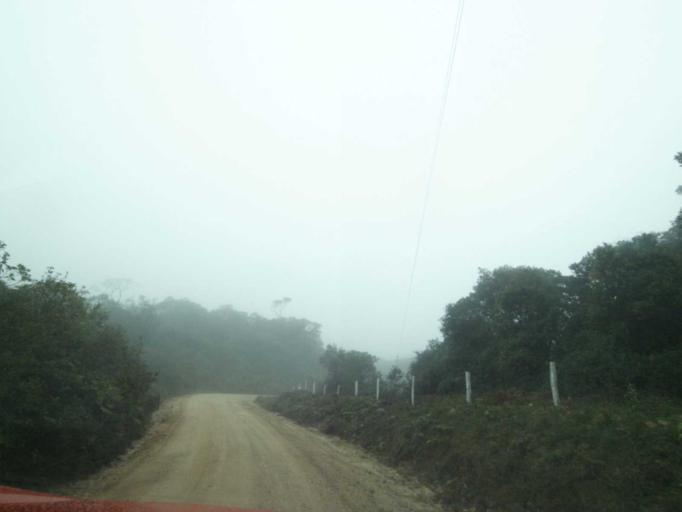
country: BR
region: Santa Catarina
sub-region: Anitapolis
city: Anitapolis
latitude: -27.9067
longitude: -49.1658
